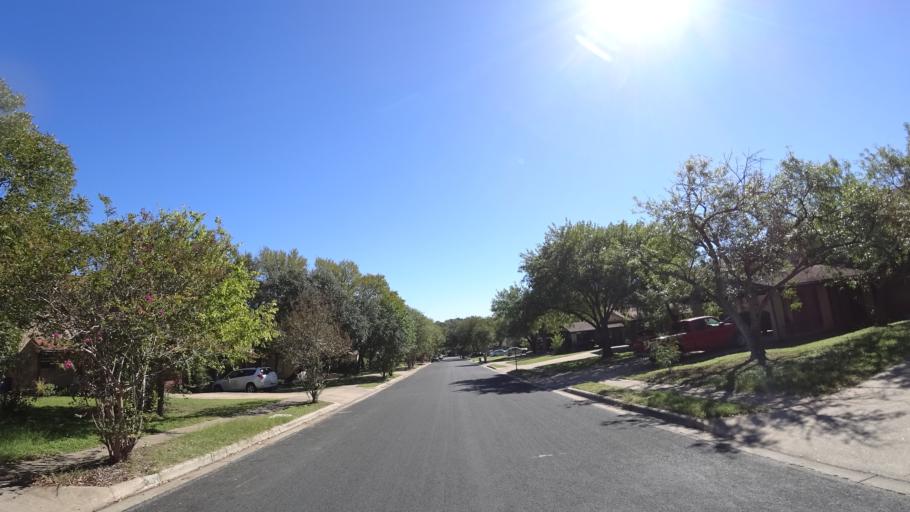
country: US
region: Texas
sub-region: Travis County
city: Rollingwood
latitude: 30.2403
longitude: -97.7744
